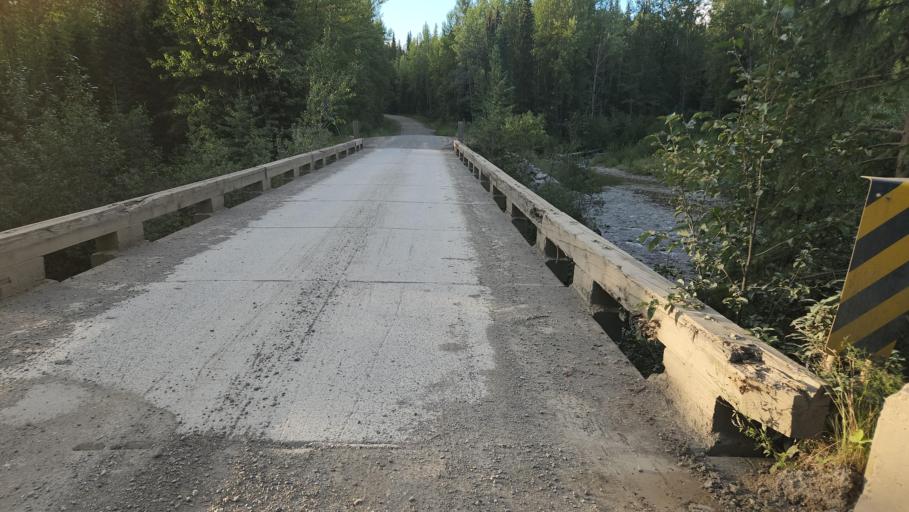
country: CA
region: British Columbia
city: Quesnel
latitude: 53.0174
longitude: -122.0820
